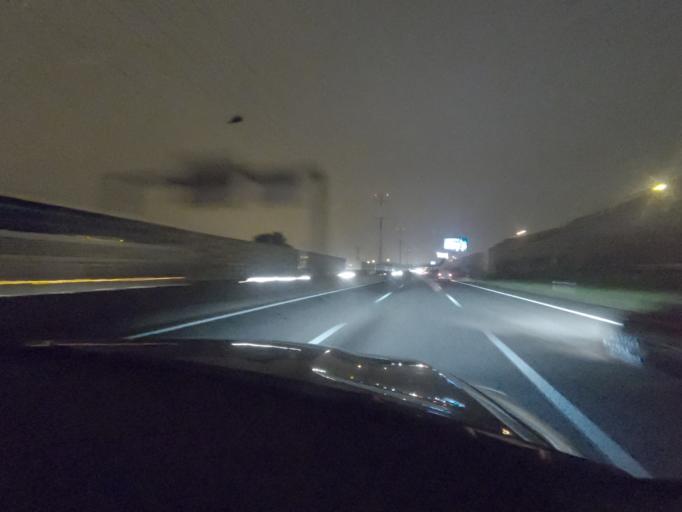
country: PT
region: Lisbon
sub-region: Loures
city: Santa Iria da Azoia
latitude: 38.8377
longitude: -9.0955
